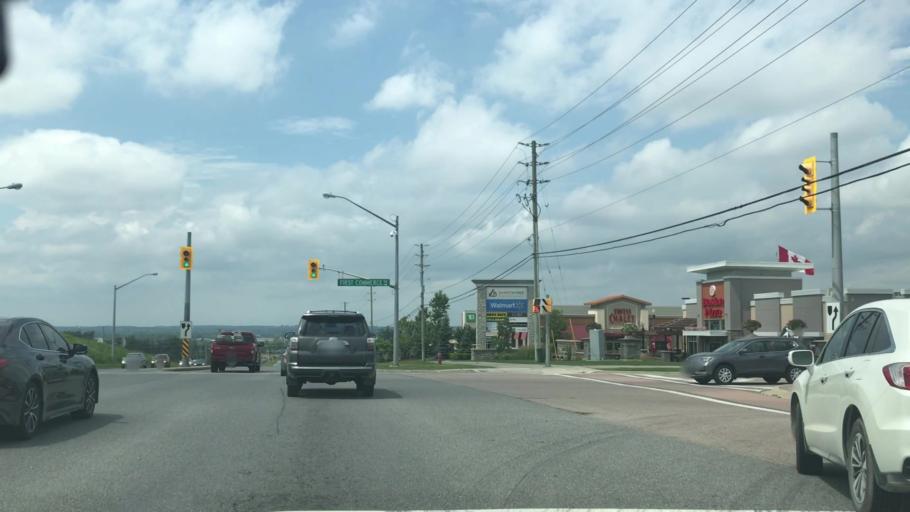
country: CA
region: Ontario
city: Newmarket
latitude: 44.0116
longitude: -79.4143
